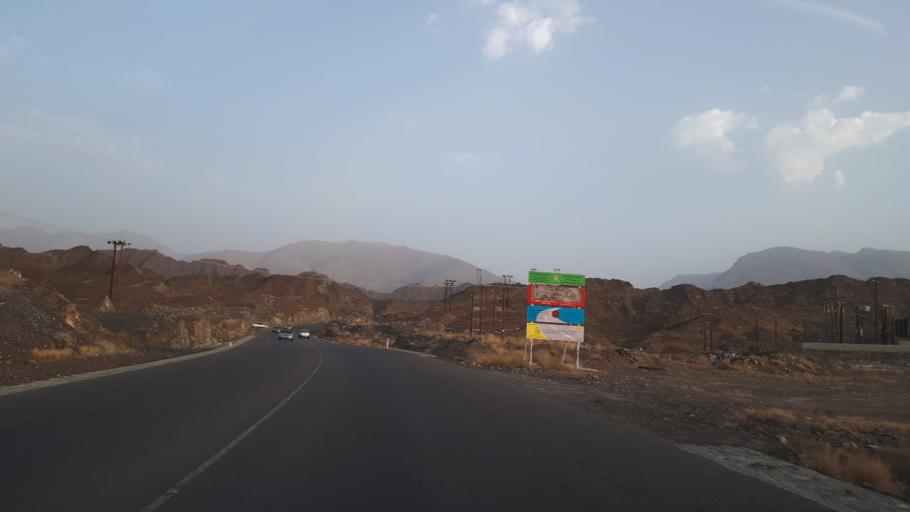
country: OM
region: Al Batinah
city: Rustaq
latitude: 23.4200
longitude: 57.3002
